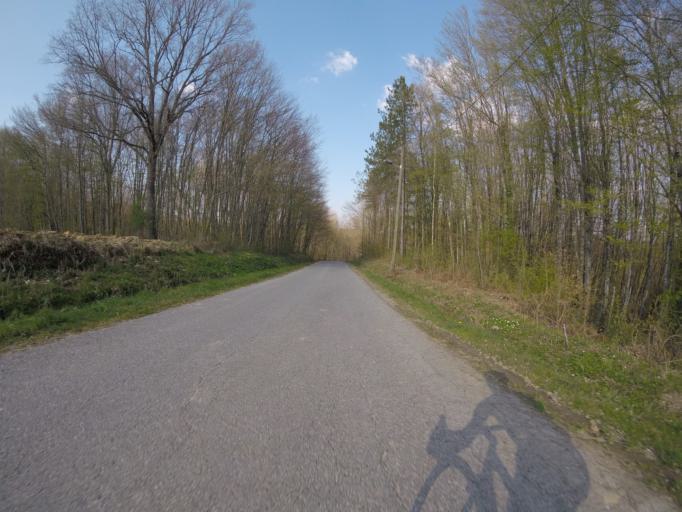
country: HR
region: Sisacko-Moslavacka
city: Gvozd
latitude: 45.4951
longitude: 15.9883
